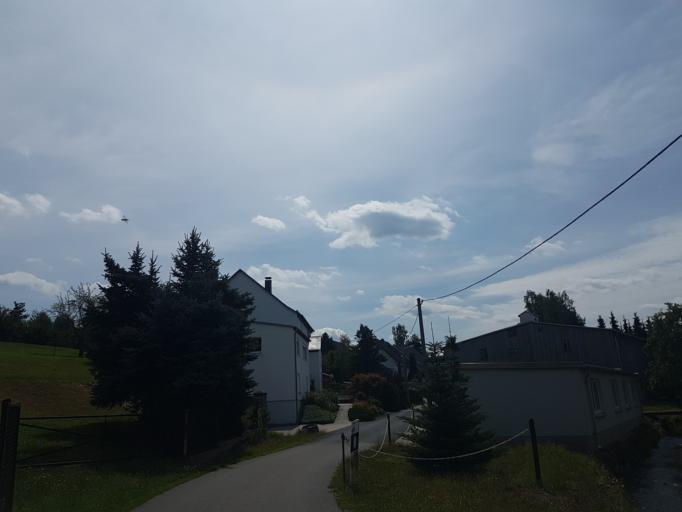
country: DE
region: Saxony
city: Freiberg
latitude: 50.8907
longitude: 13.3589
